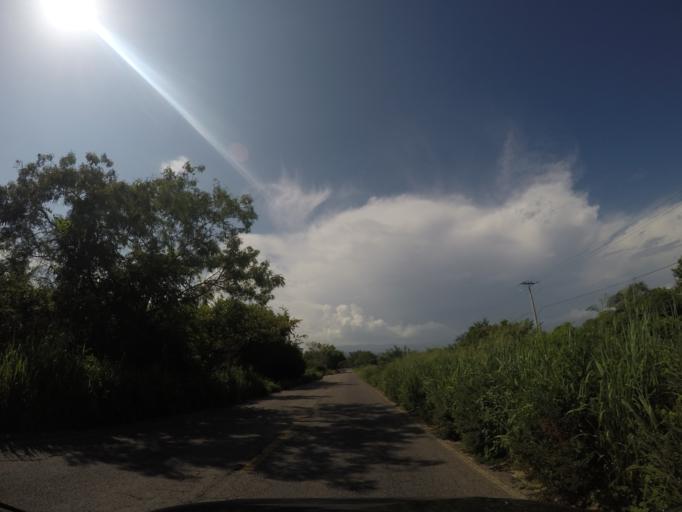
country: MX
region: Oaxaca
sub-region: San Pedro Mixtepec -Dto. 22 -
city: Puerto Escondido
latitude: 15.9055
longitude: -97.1177
